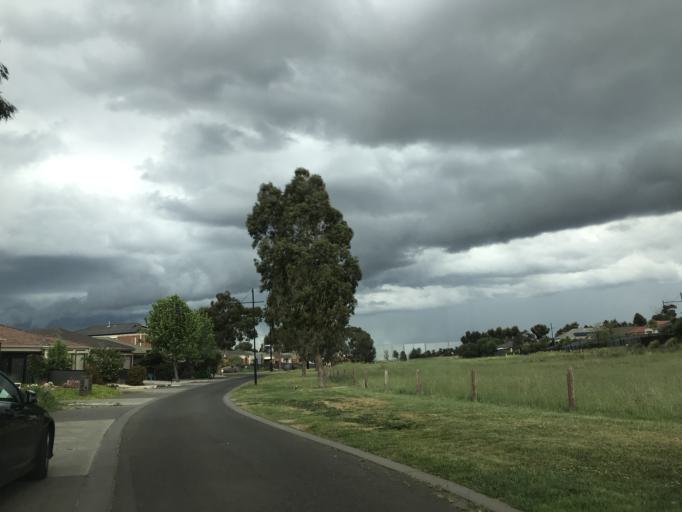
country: AU
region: Victoria
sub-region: Brimbank
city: Derrimut
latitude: -37.7952
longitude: 144.7691
